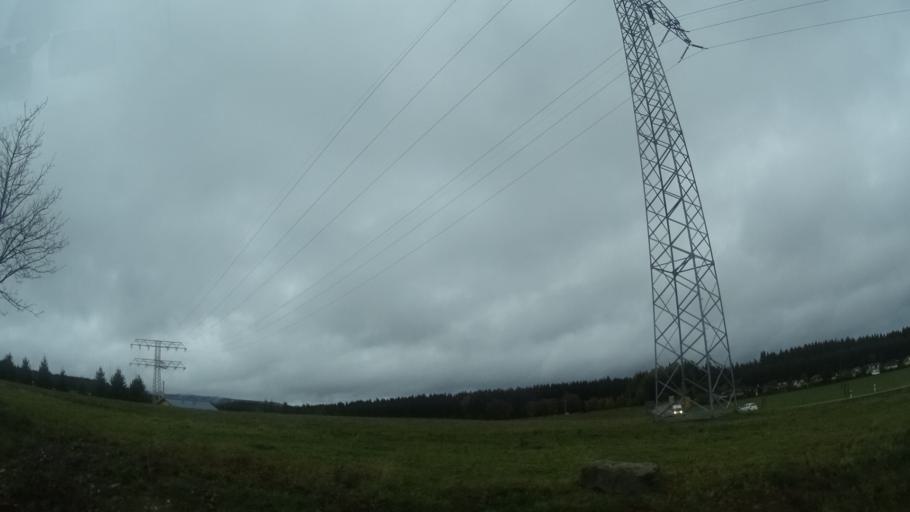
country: DE
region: Thuringia
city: Neuhaus am Rennweg
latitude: 50.5207
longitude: 11.1452
